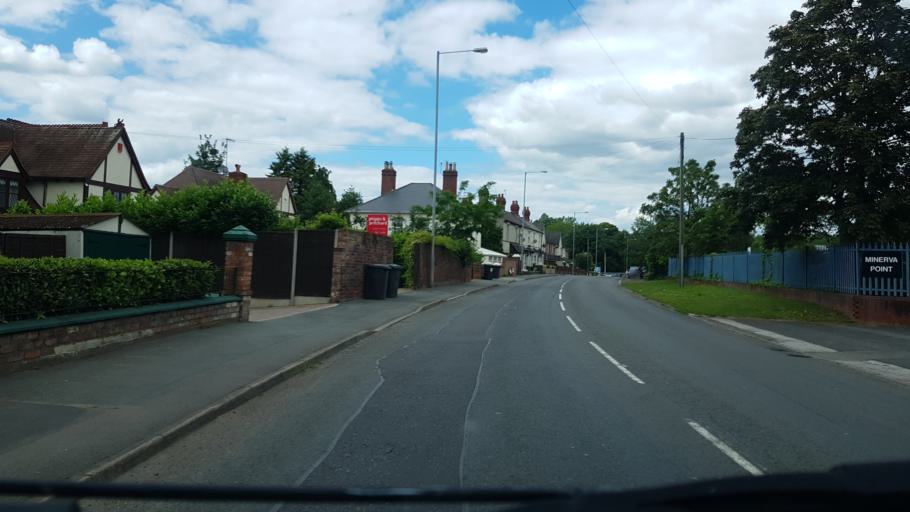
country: GB
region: England
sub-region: Worcestershire
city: Stourport-on-Severn
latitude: 52.3381
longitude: -2.2706
